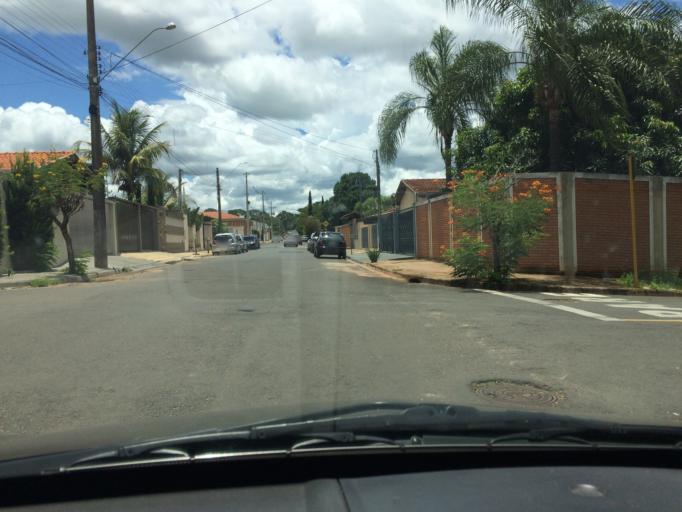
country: BR
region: Sao Paulo
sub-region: Casa Branca
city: Casa Branca
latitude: -21.7796
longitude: -47.0842
